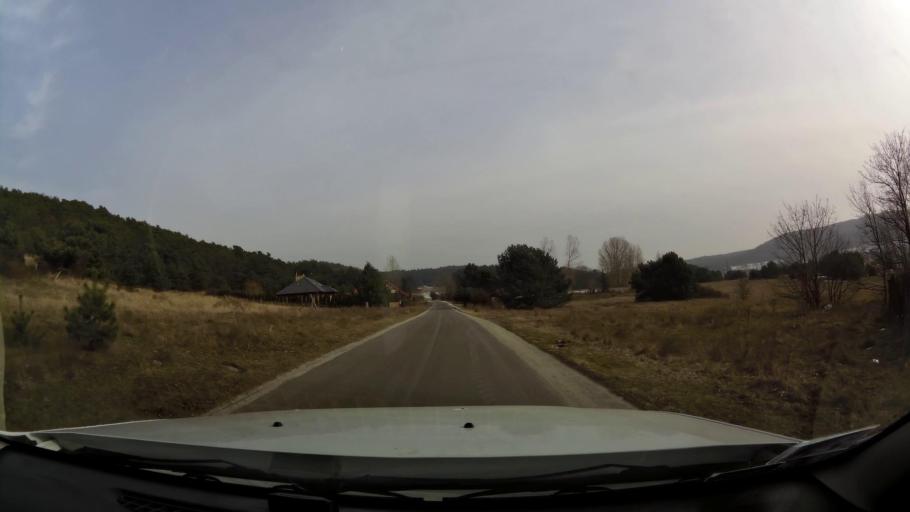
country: PL
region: West Pomeranian Voivodeship
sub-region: Powiat kamienski
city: Miedzyzdroje
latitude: 53.8873
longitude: 14.4416
